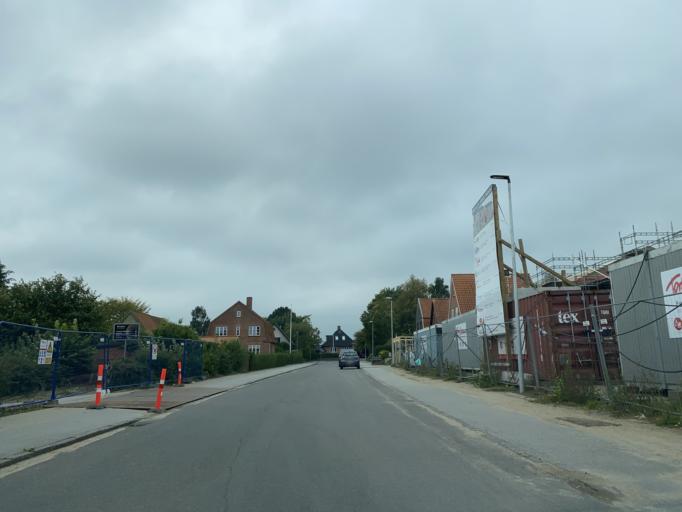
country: DK
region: South Denmark
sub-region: Haderslev Kommune
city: Haderslev
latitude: 55.2532
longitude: 9.4709
